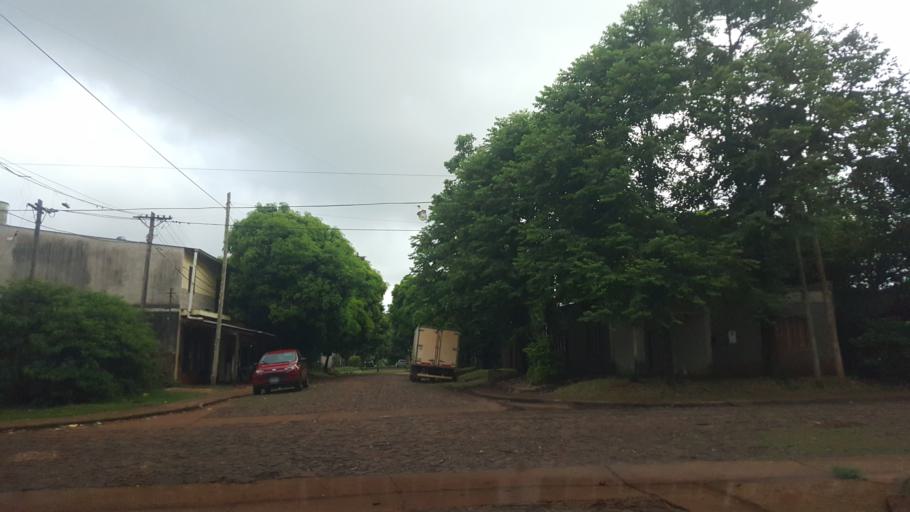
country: AR
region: Misiones
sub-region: Departamento de Capital
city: Posadas
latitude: -27.3865
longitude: -55.9202
